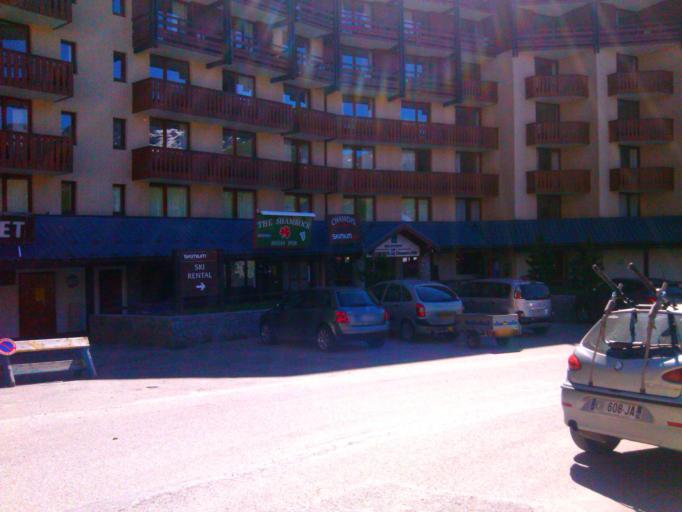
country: FR
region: Rhone-Alpes
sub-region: Departement de la Savoie
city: Val Thorens
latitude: 45.2968
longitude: 6.5810
